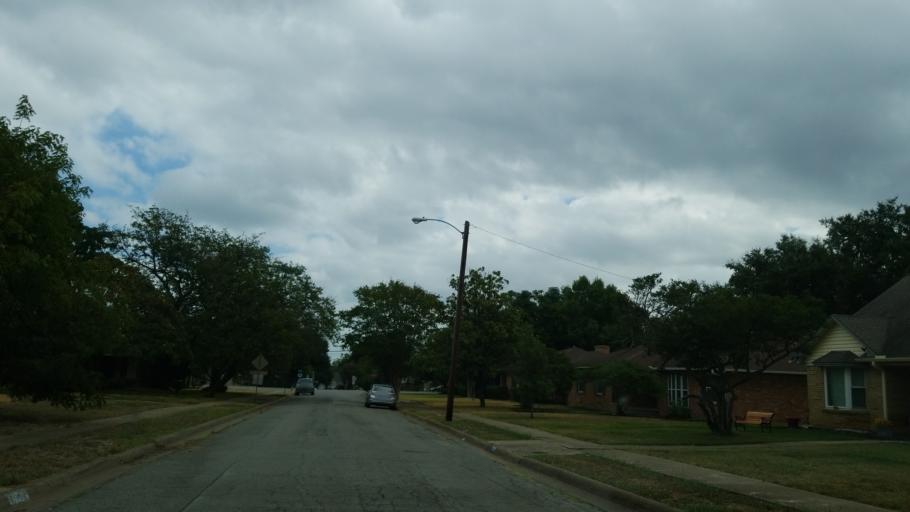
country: US
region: Texas
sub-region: Dallas County
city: Richardson
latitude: 32.9363
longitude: -96.7703
